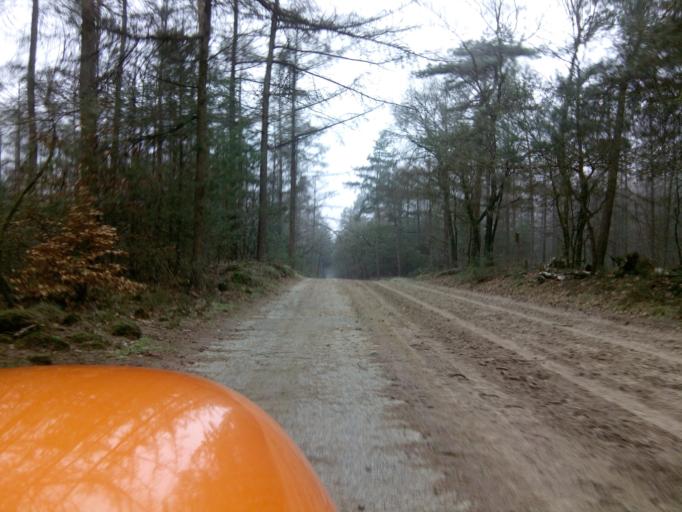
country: NL
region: Gelderland
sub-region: Gemeente Barneveld
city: Voorthuizen
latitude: 52.2184
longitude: 5.6368
